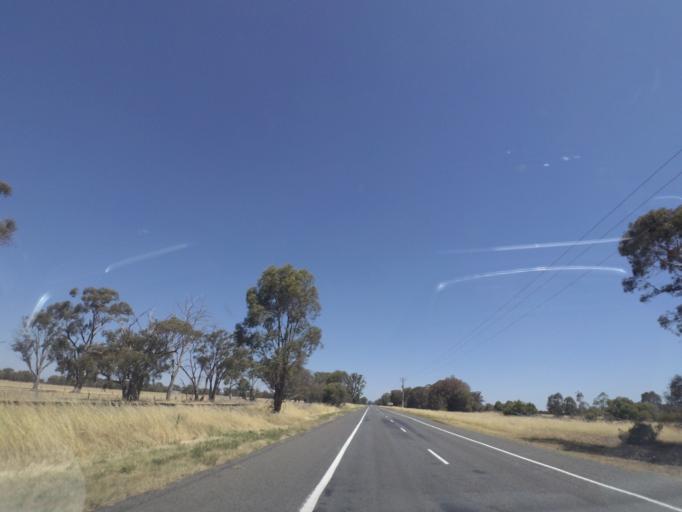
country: AU
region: Victoria
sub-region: Greater Shepparton
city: Shepparton
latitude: -36.2125
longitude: 145.4319
